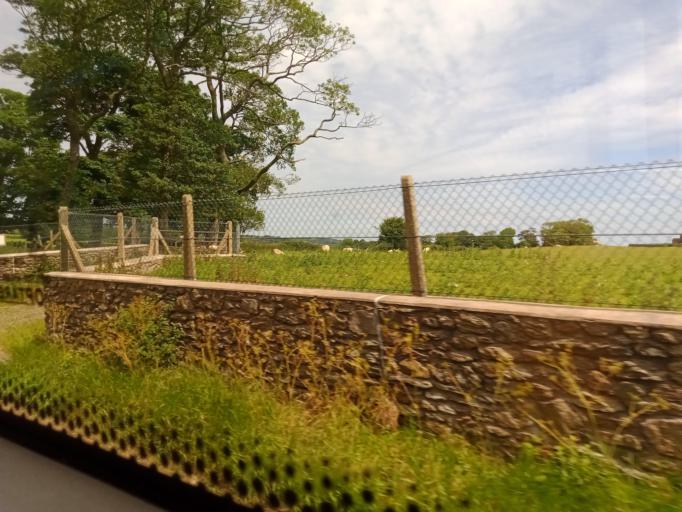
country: GB
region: Wales
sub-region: Anglesey
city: Beaumaris
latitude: 53.2719
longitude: -4.1155
